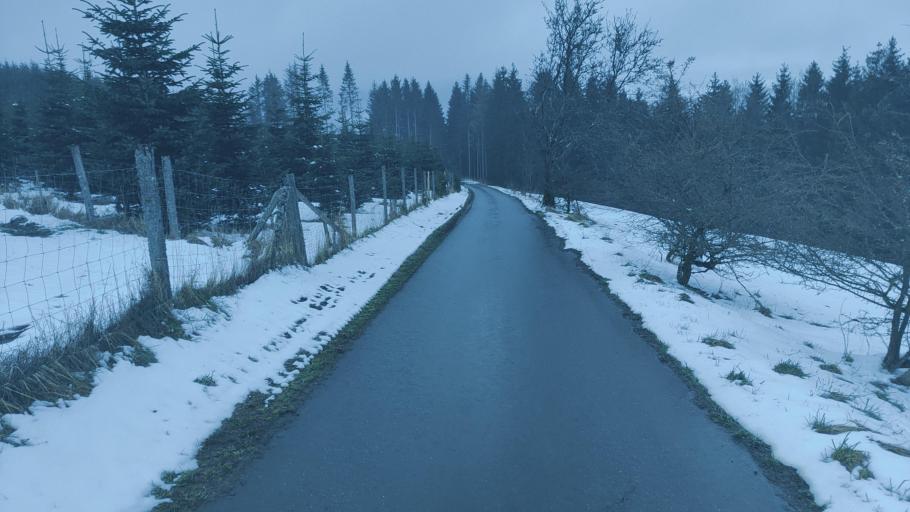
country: DE
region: North Rhine-Westphalia
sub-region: Regierungsbezirk Arnsberg
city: Bad Berleburg
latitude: 51.1537
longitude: 8.4184
